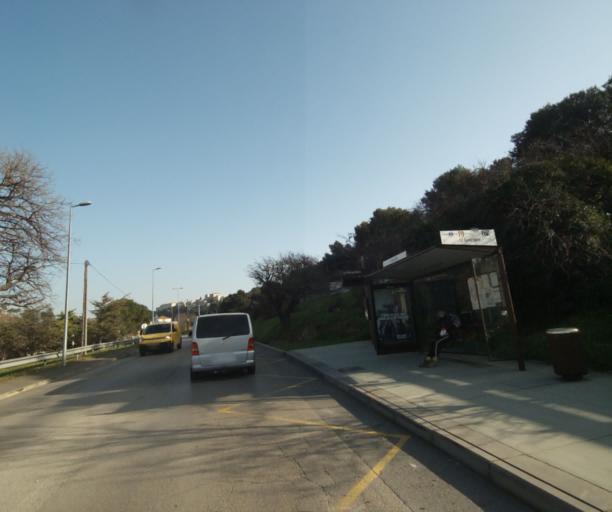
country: FR
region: Provence-Alpes-Cote d'Azur
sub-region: Departement des Bouches-du-Rhone
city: Les Pennes-Mirabeau
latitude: 43.4130
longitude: 5.3020
